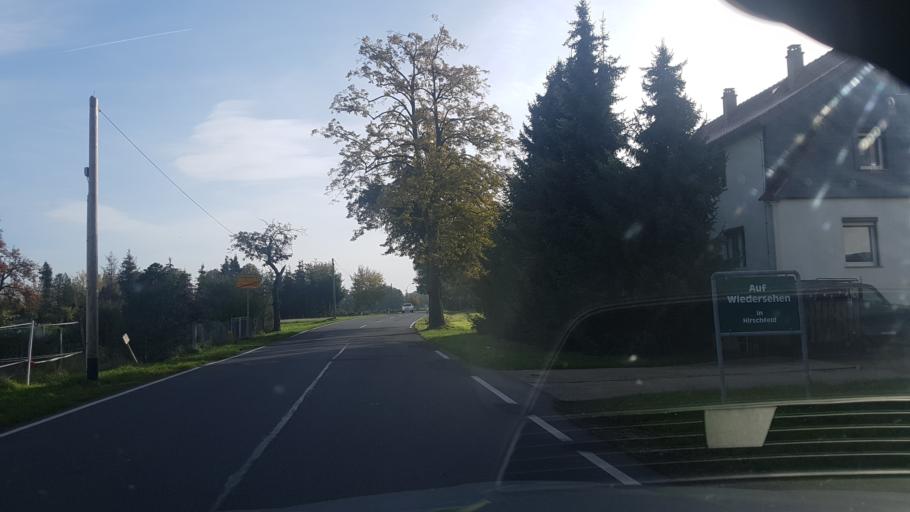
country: DE
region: Brandenburg
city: Hirschfeld
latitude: 51.3855
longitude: 13.6228
